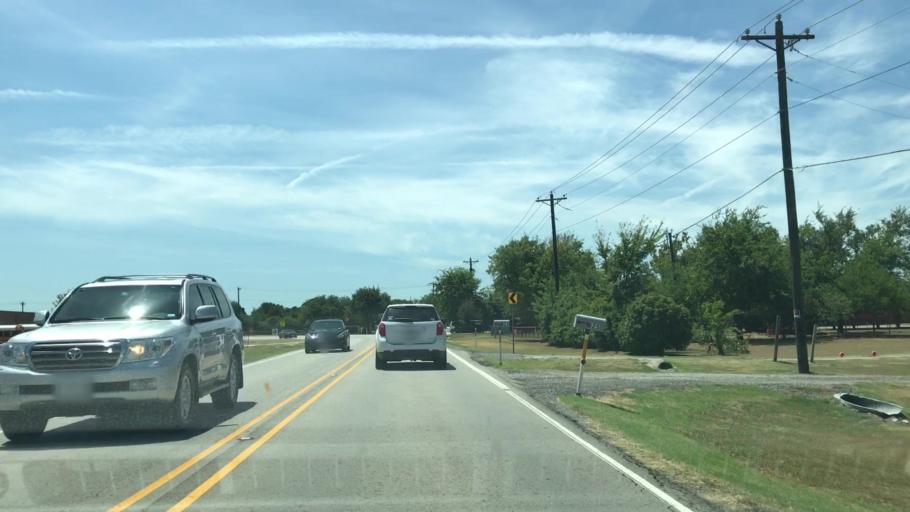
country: US
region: Texas
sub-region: Collin County
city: Lucas
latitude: 33.0946
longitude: -96.5942
